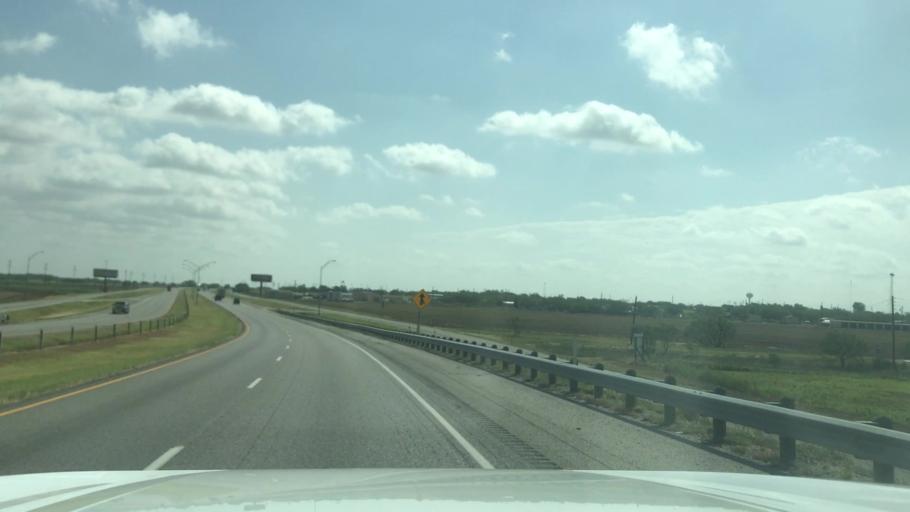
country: US
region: Texas
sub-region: Taylor County
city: Merkel
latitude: 32.4748
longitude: -100.0294
